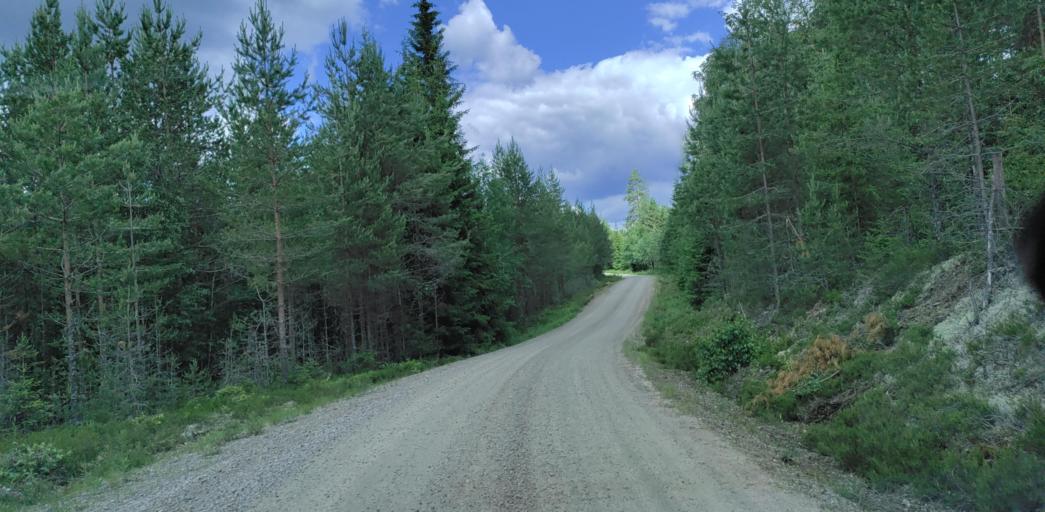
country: SE
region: Vaermland
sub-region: Hagfors Kommun
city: Ekshaerad
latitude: 60.0702
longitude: 13.2904
